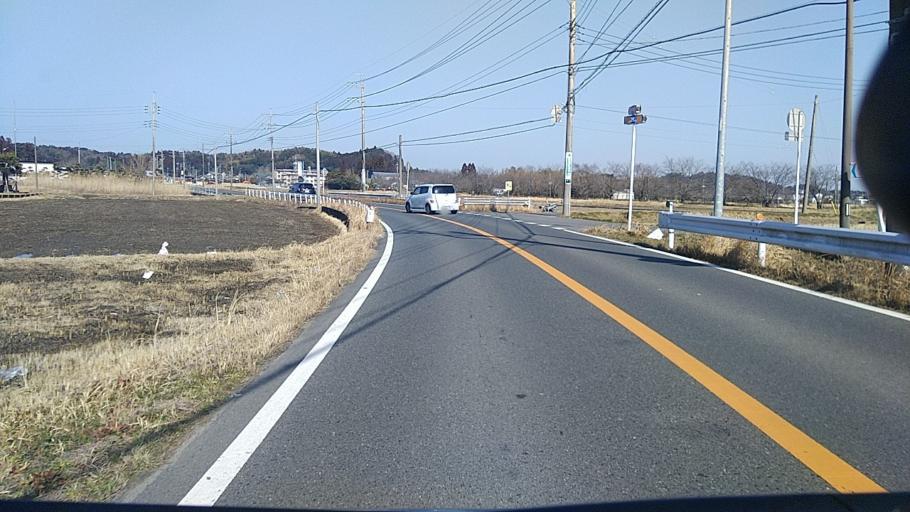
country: JP
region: Chiba
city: Mobara
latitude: 35.4188
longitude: 140.2646
